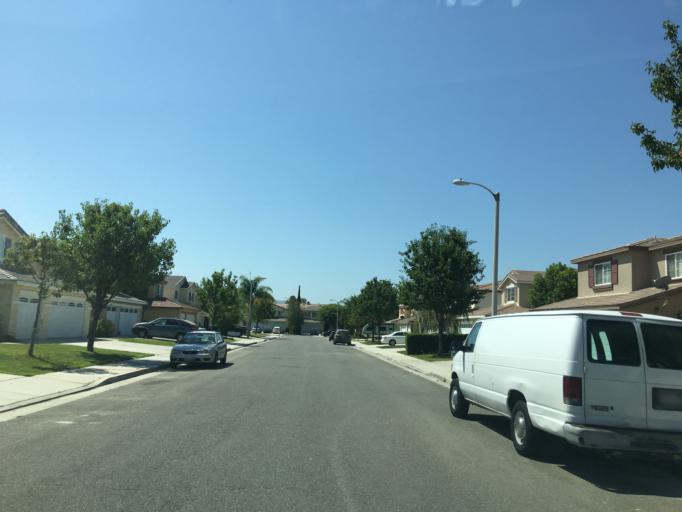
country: US
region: California
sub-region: Los Angeles County
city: Castaic
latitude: 34.4717
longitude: -118.6449
